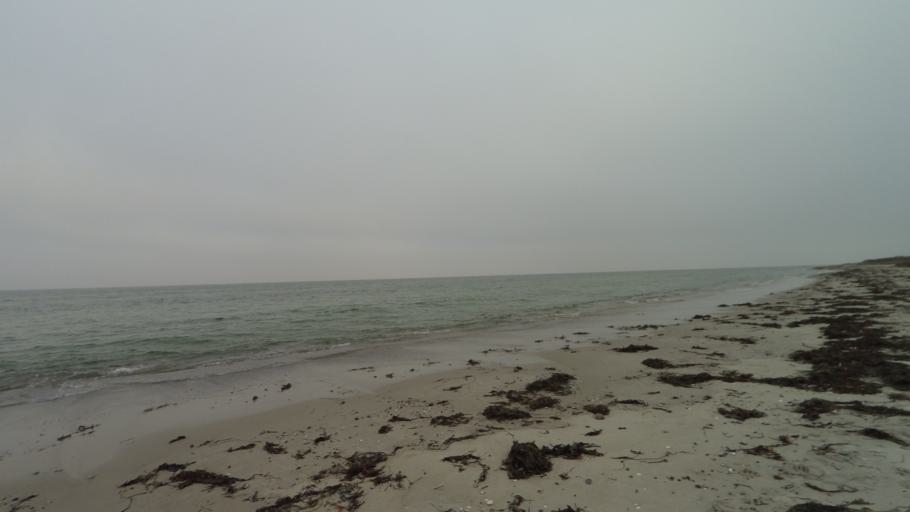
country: DK
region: Central Jutland
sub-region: Arhus Kommune
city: Malling
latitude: 55.9673
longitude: 10.2606
